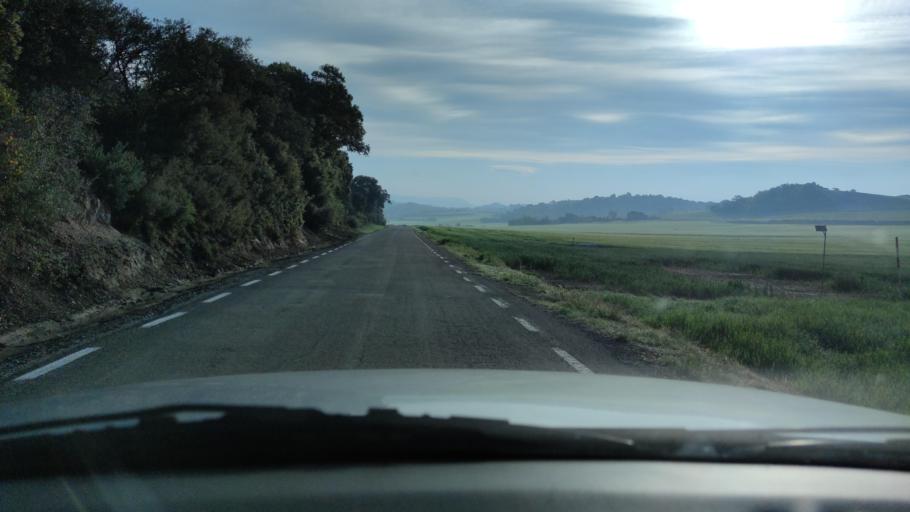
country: ES
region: Catalonia
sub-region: Provincia de Lleida
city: Artesa de Segre
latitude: 41.8583
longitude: 1.0629
